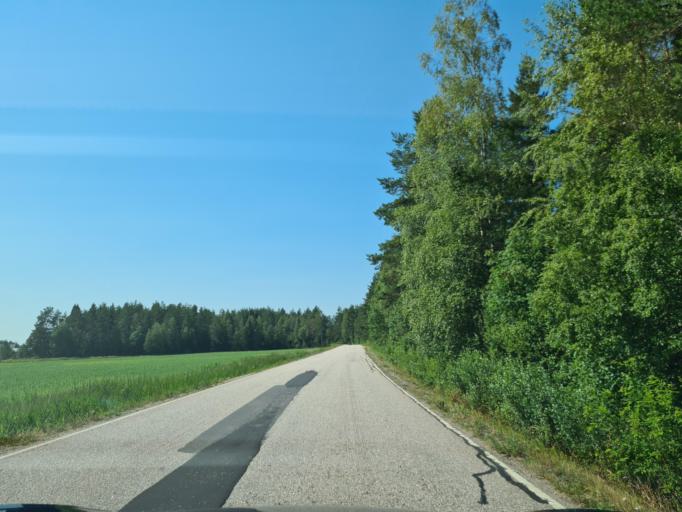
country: FI
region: Varsinais-Suomi
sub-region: Loimaa
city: Aura
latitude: 60.6032
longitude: 22.5996
